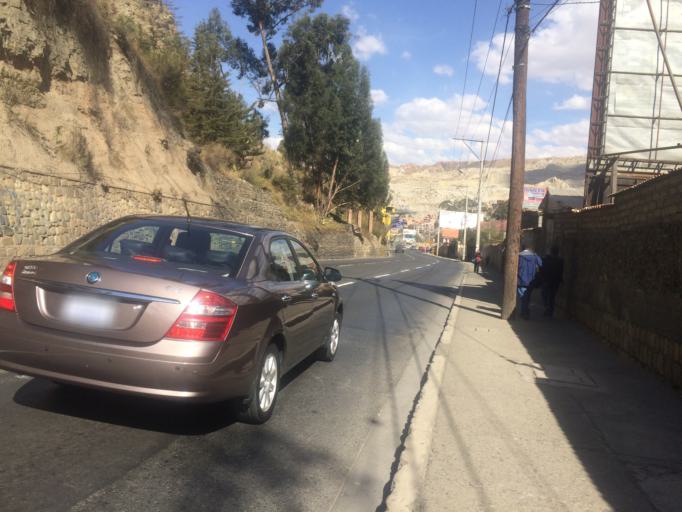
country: BO
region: La Paz
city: La Paz
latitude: -16.5170
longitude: -68.1168
